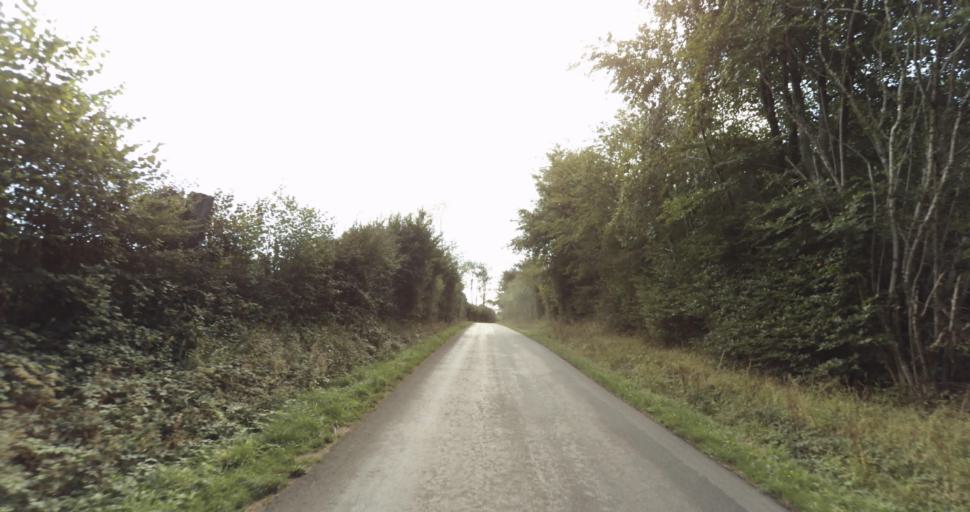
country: FR
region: Lower Normandy
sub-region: Departement de l'Orne
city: Sainte-Gauburge-Sainte-Colombe
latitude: 48.7559
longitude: 0.4103
